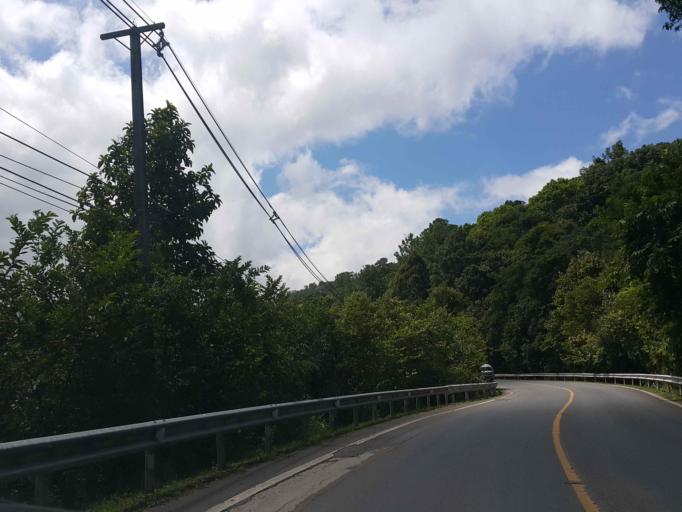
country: TH
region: Chiang Mai
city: Chom Thong
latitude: 18.5441
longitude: 98.5465
